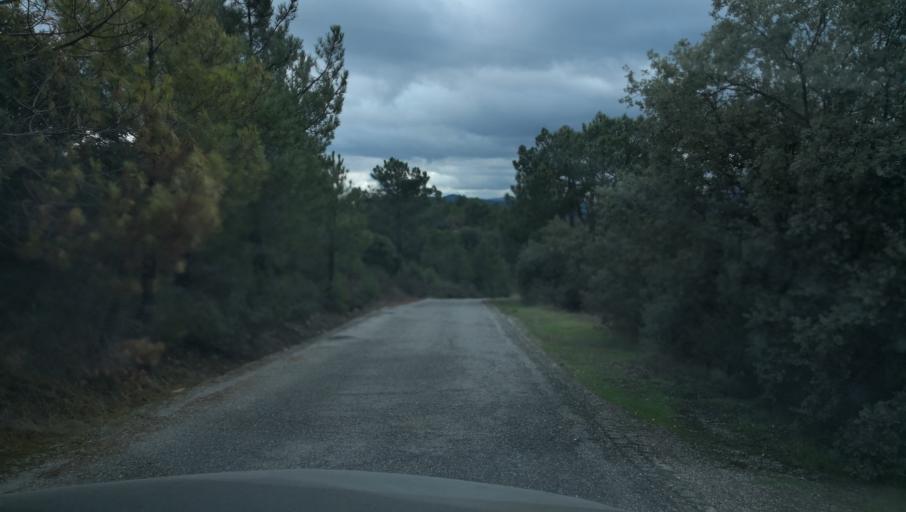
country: PT
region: Vila Real
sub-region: Sabrosa
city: Vilela
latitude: 41.1865
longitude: -7.5741
